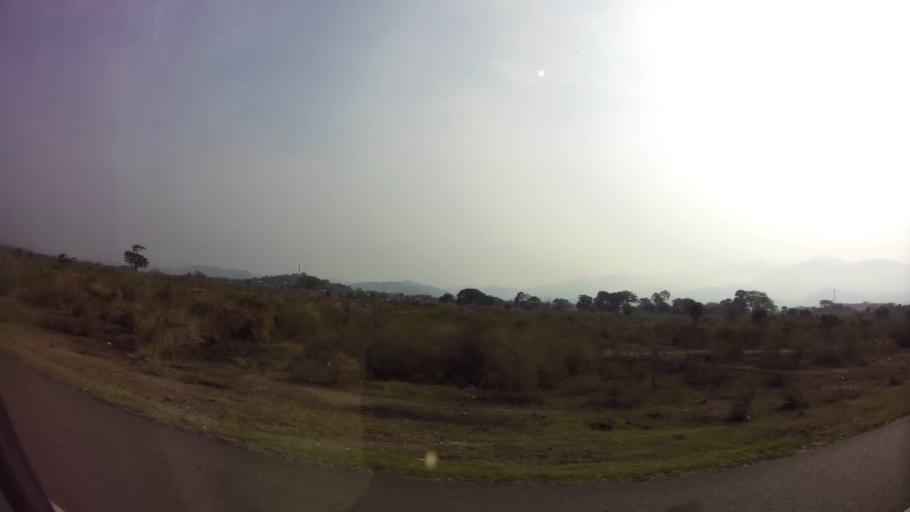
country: HN
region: Comayagua
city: Comayagua
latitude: 14.4304
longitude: -87.6441
